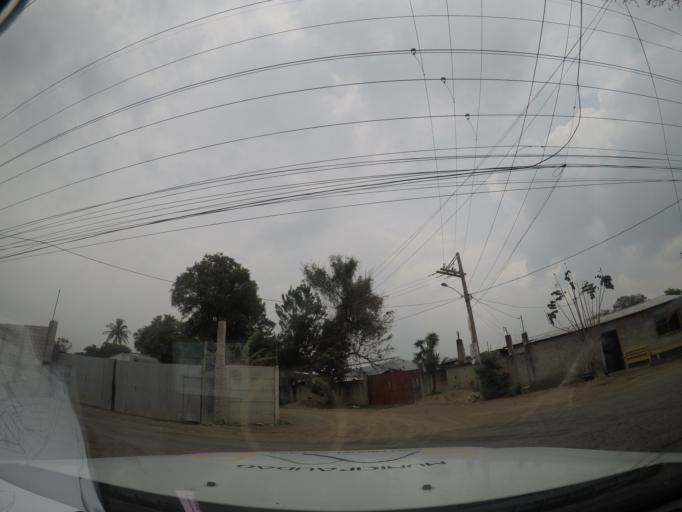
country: GT
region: Guatemala
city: Petapa
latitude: 14.5120
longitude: -90.5542
